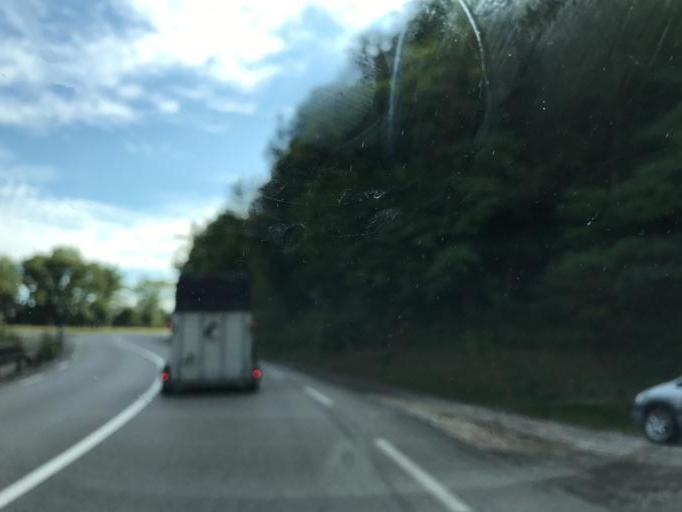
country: FR
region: Rhone-Alpes
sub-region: Departement de l'Ain
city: Collonges
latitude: 46.1200
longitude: 5.8902
